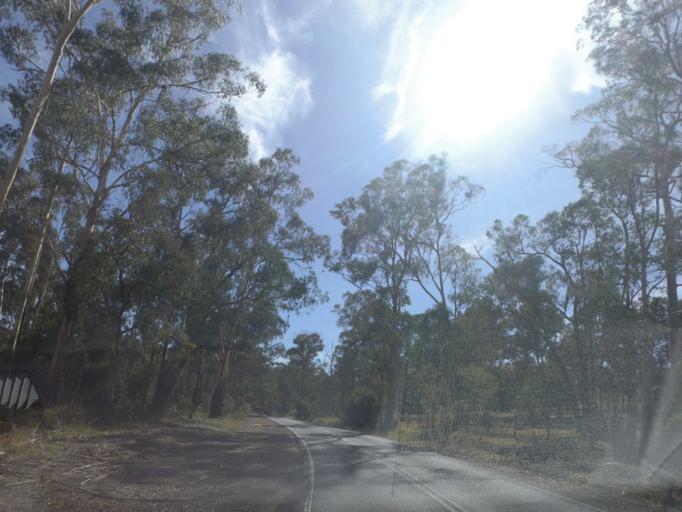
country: AU
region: Victoria
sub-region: Nillumbik
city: Saint Andrews
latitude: -37.6126
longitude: 145.2343
